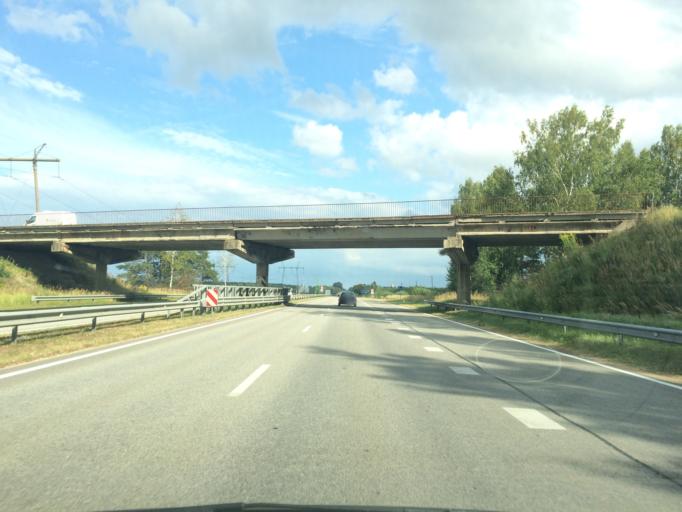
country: LV
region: Salaspils
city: Salaspils
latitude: 56.8462
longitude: 24.3957
